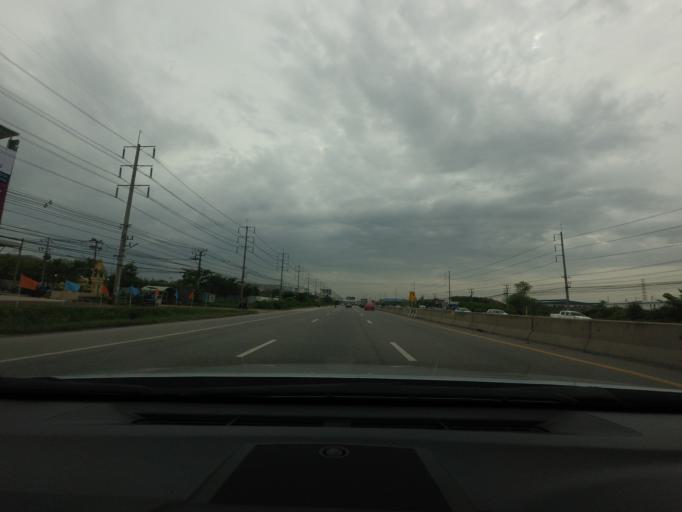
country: TH
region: Samut Sakhon
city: Ban Phaeo
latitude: 13.5107
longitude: 100.1413
